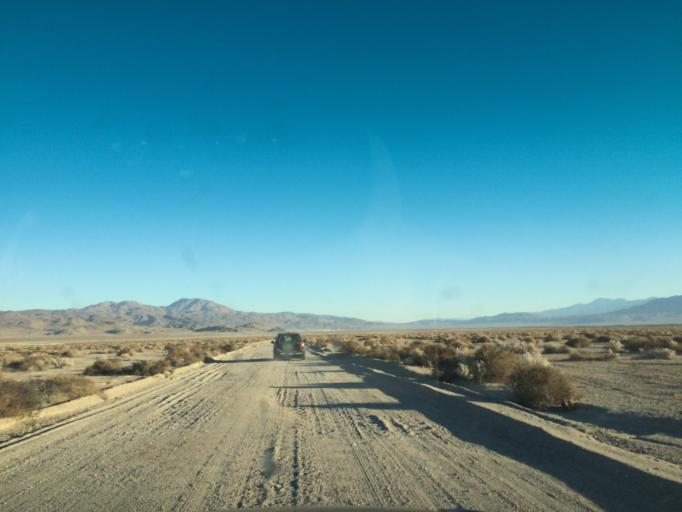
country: US
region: California
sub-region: San Bernardino County
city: Searles Valley
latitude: 35.6408
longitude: -117.3760
